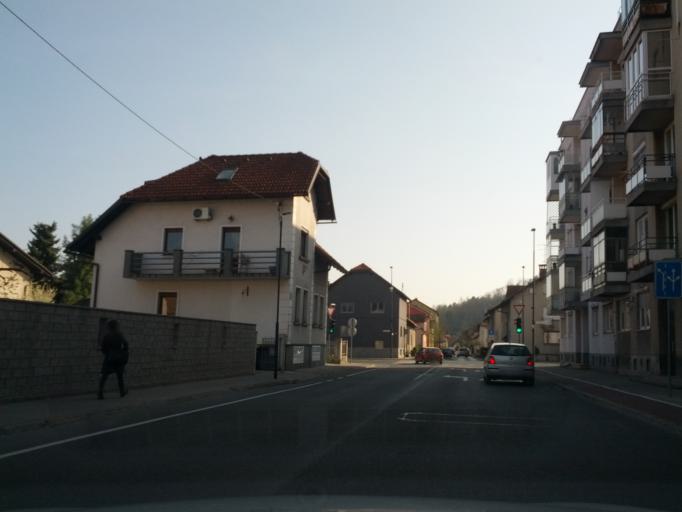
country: SI
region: Ljubljana
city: Ljubljana
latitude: 46.0676
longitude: 14.4969
